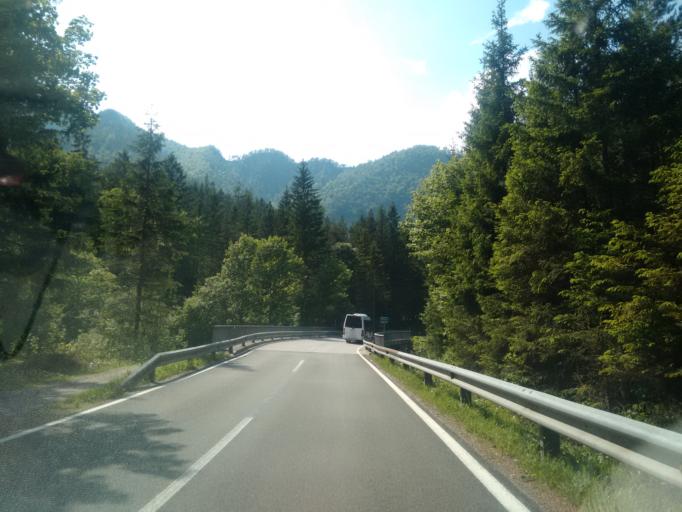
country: AT
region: Upper Austria
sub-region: Politischer Bezirk Kirchdorf an der Krems
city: Rossleithen
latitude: 47.7447
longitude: 14.1676
